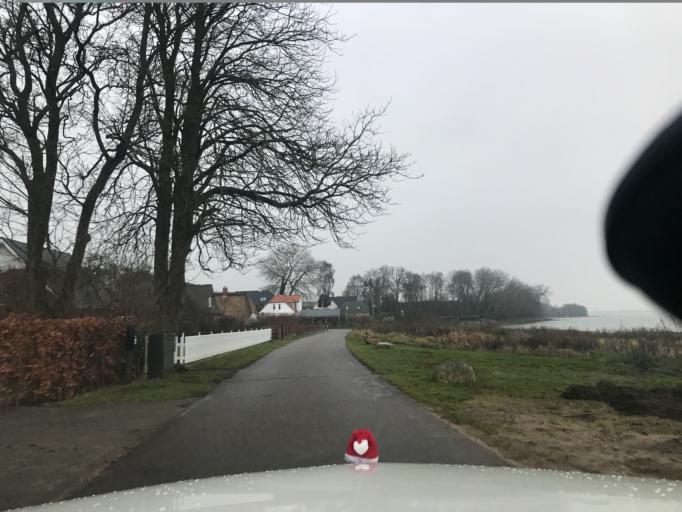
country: DK
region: South Denmark
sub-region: Sonderborg Kommune
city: Grasten
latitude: 54.8810
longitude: 9.5673
